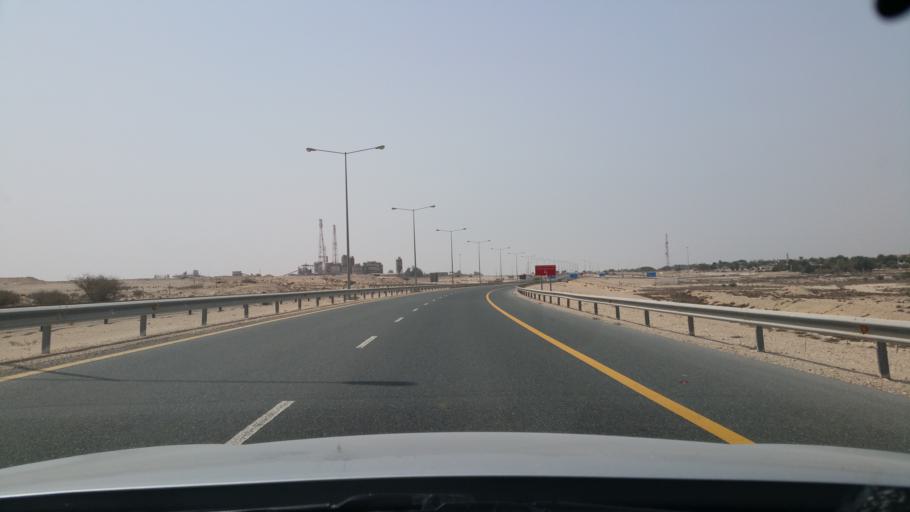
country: QA
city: Umm Bab
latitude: 25.2179
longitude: 50.8077
